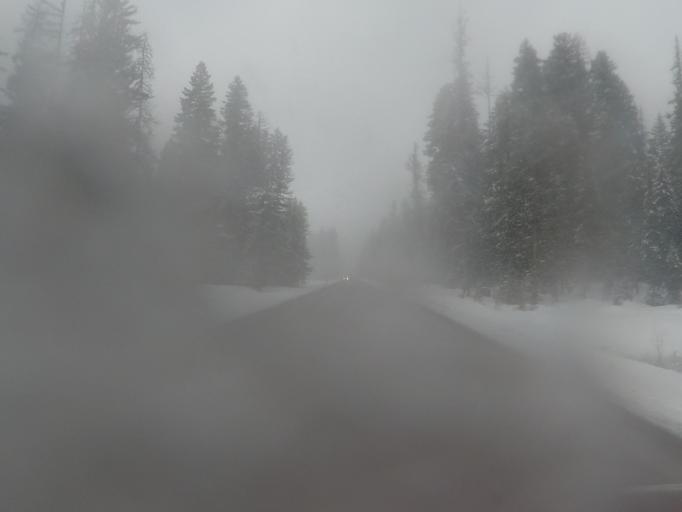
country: US
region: Montana
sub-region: Missoula County
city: Seeley Lake
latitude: 47.4343
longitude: -113.6686
